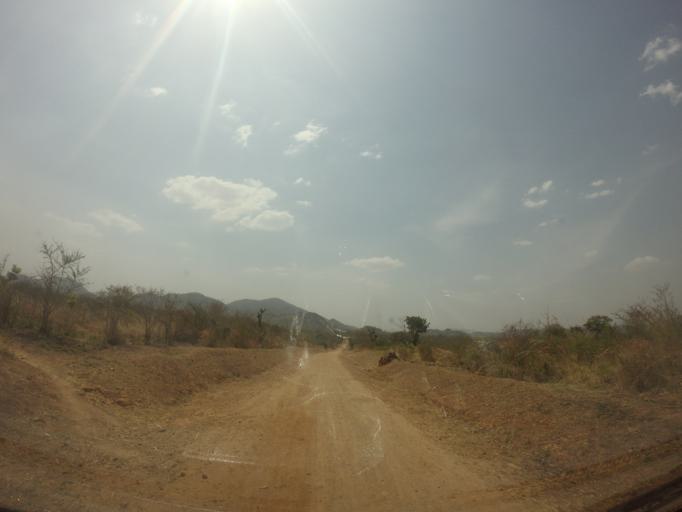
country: UG
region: Northern Region
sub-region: Arua District
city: Arua
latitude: 2.8968
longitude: 31.1206
